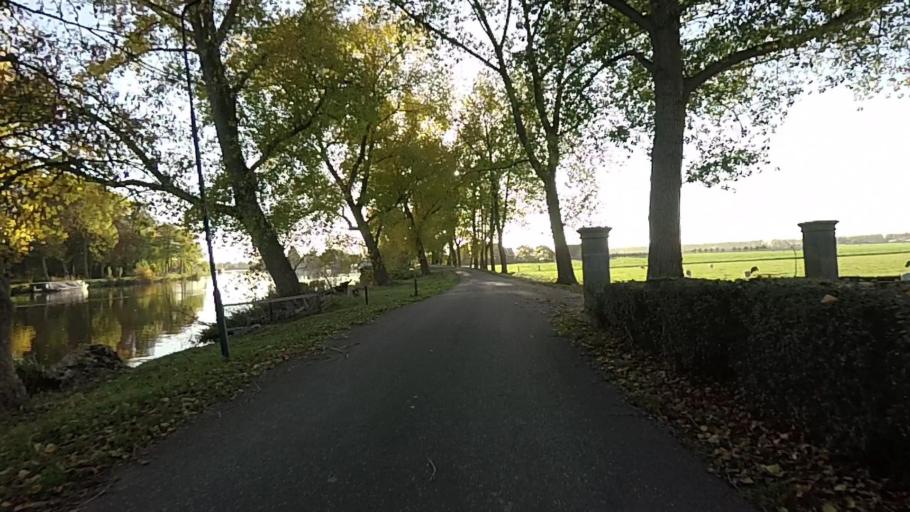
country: NL
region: Utrecht
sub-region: Stichtse Vecht
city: Vreeland
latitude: 52.2392
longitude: 5.0355
